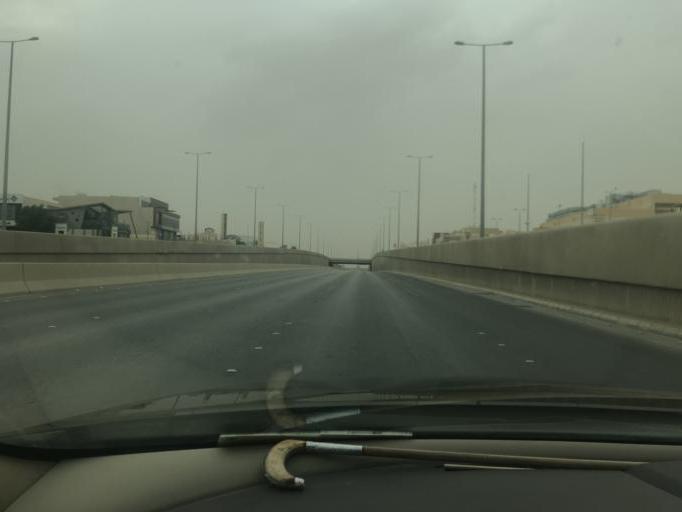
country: SA
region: Ar Riyad
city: Riyadh
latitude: 24.7768
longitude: 46.7083
